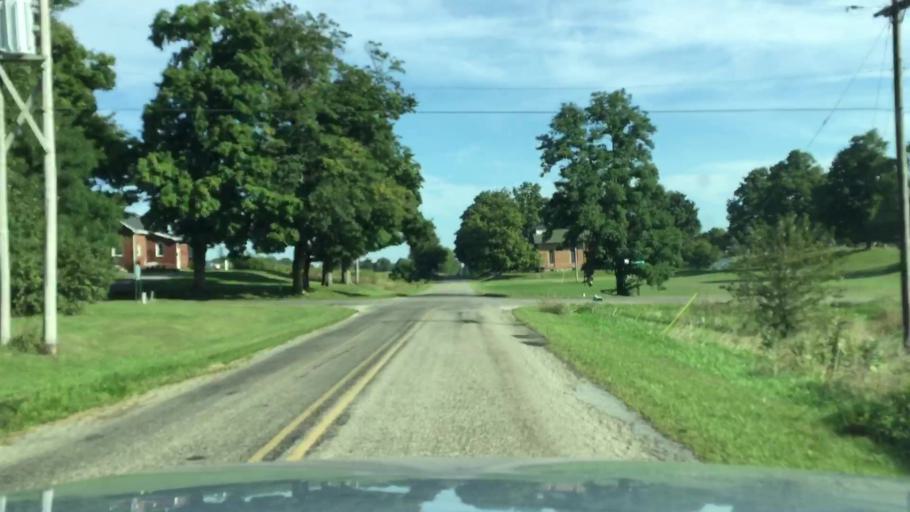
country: US
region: Michigan
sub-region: Lenawee County
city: Hudson
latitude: 41.8835
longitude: -84.4202
